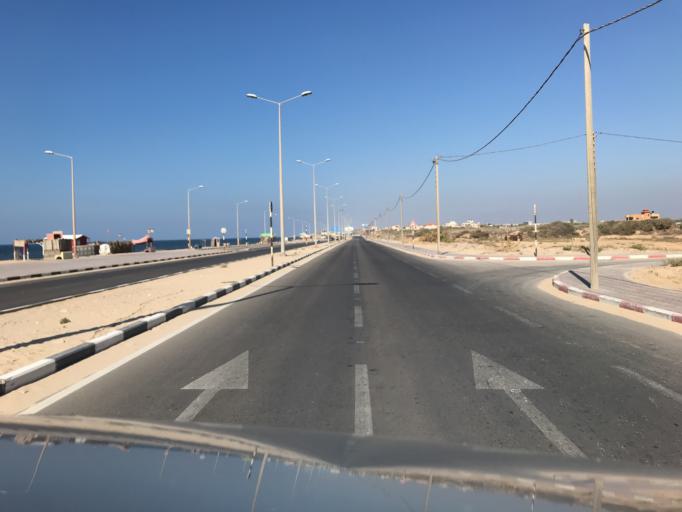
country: PS
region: Gaza Strip
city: An Nusayrat
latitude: 31.4721
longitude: 34.3842
